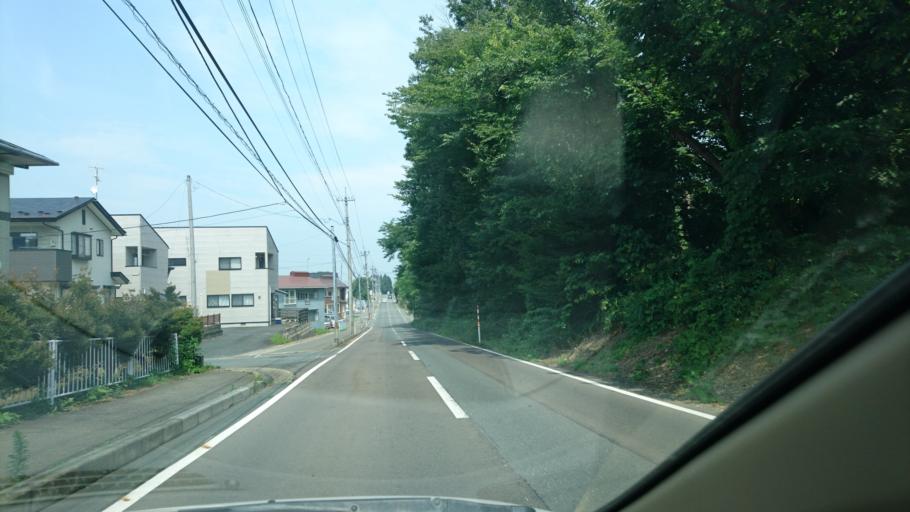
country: JP
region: Iwate
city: Kitakami
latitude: 39.2647
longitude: 141.0896
